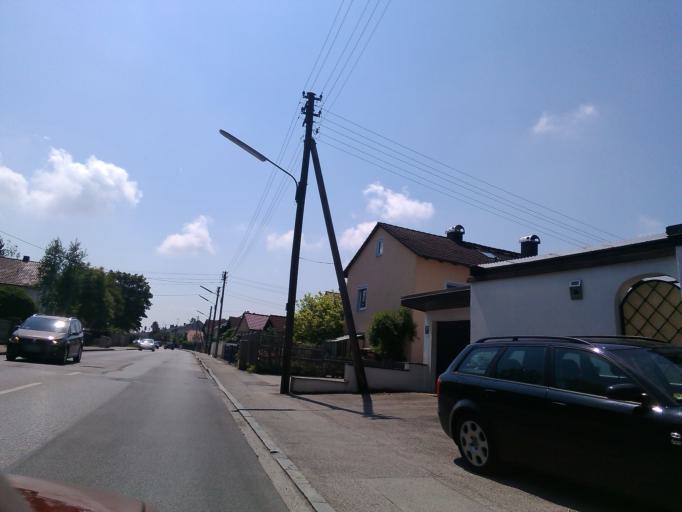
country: DE
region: Bavaria
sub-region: Upper Bavaria
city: Olching
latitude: 48.1996
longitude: 11.3240
